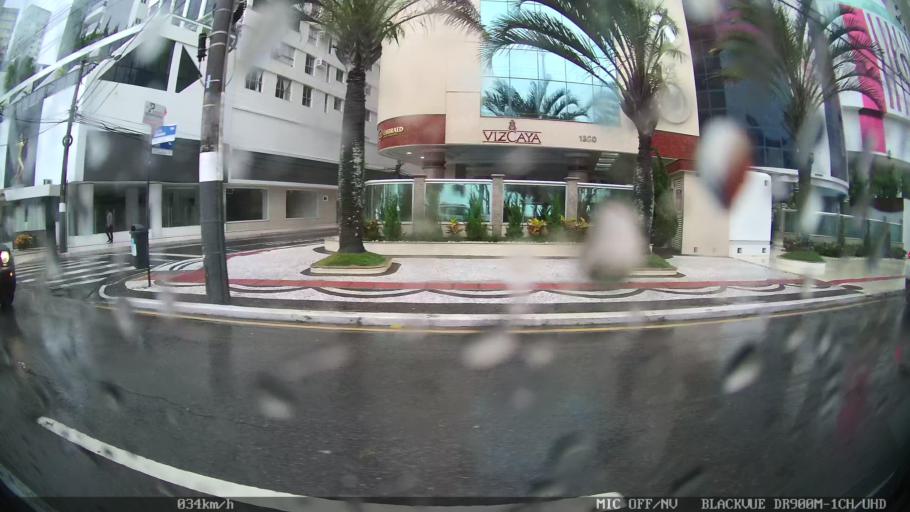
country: BR
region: Santa Catarina
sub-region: Balneario Camboriu
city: Balneario Camboriu
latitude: -26.9818
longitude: -48.6344
